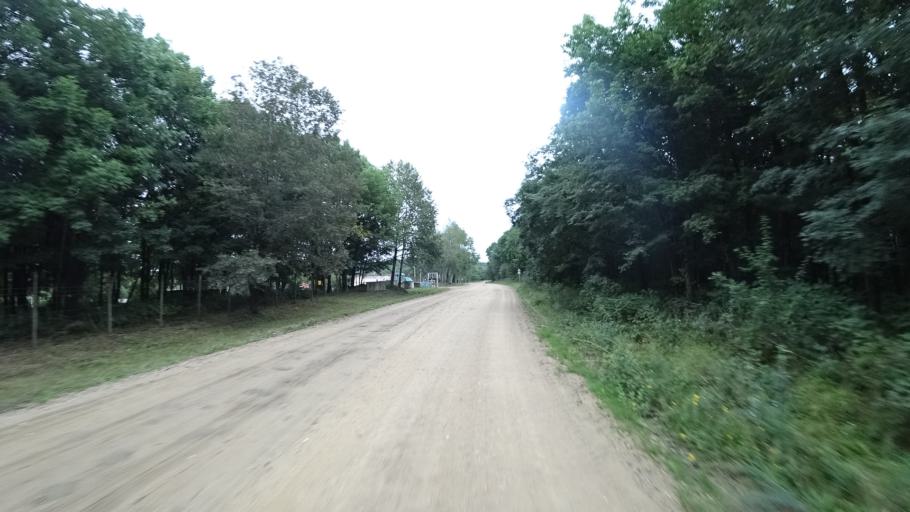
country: RU
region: Primorskiy
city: Rettikhovka
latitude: 44.1768
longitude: 132.8478
